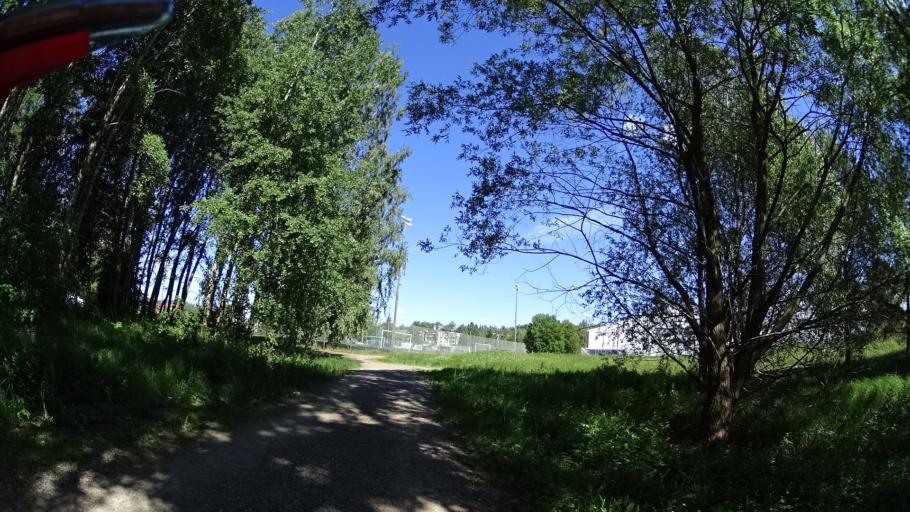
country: FI
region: Uusimaa
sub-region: Helsinki
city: Vantaa
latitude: 60.2986
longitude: 25.0258
